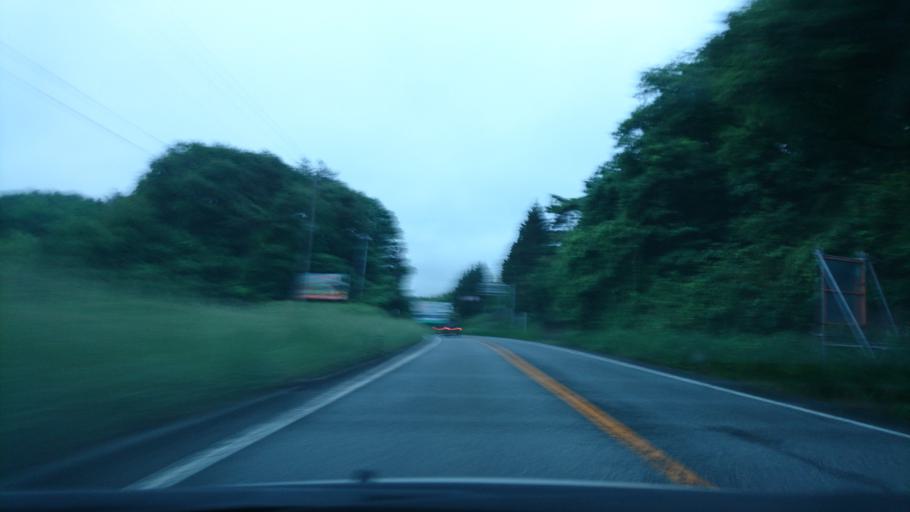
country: JP
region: Iwate
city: Ichinoseki
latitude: 38.8816
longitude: 141.1181
